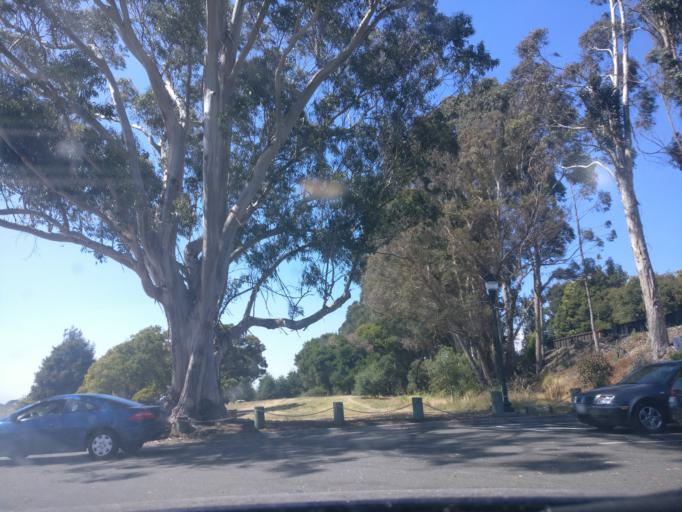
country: US
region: California
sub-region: Alameda County
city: Emeryville
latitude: 37.8517
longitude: -122.2963
